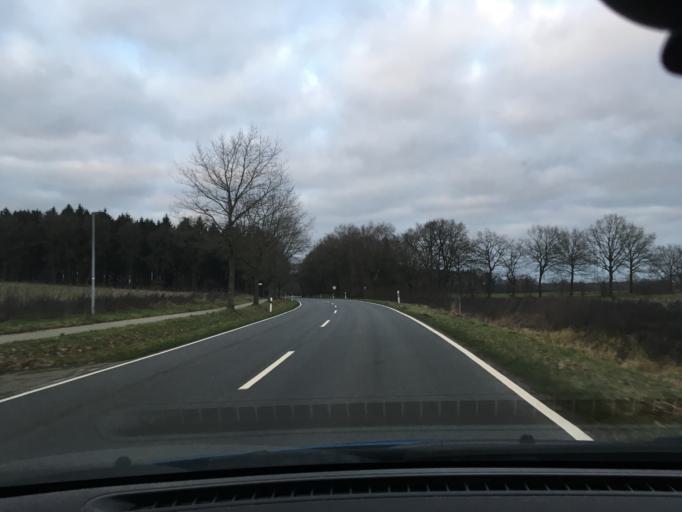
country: DE
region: Schleswig-Holstein
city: Mehlbek
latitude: 53.9920
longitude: 9.4392
